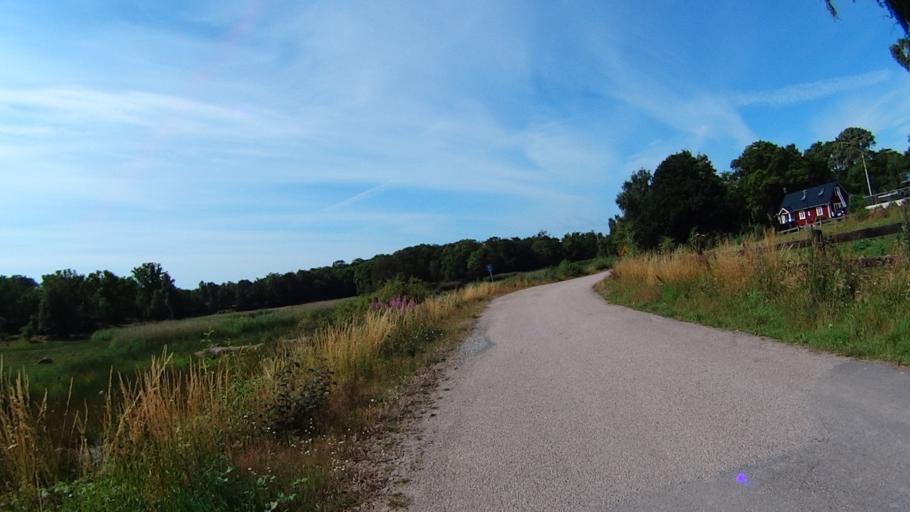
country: SE
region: Blekinge
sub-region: Ronneby Kommun
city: Brakne-Hoby
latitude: 56.1579
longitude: 15.0860
